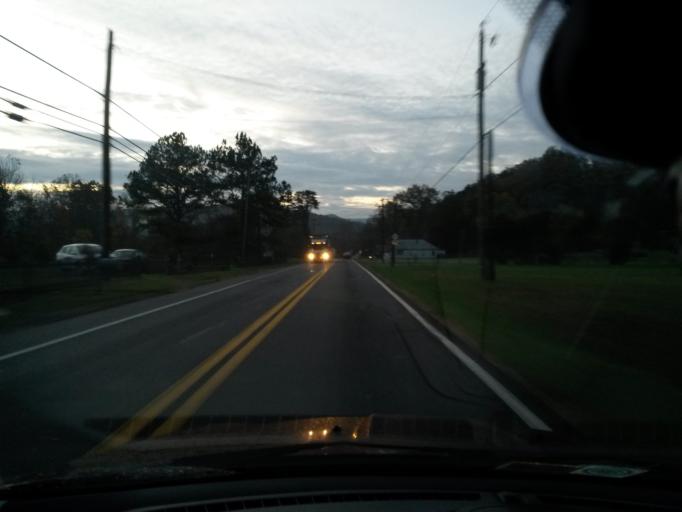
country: US
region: Virginia
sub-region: Alleghany County
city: Clifton Forge
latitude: 37.7895
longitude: -79.7834
